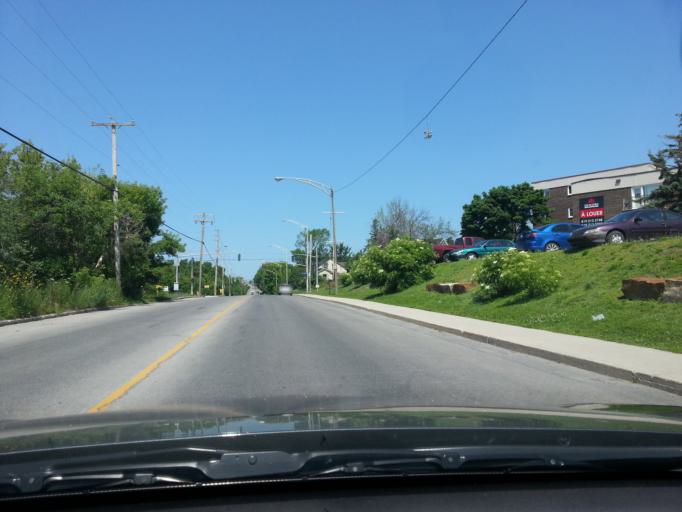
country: CA
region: Ontario
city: Bells Corners
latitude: 45.4013
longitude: -75.8542
